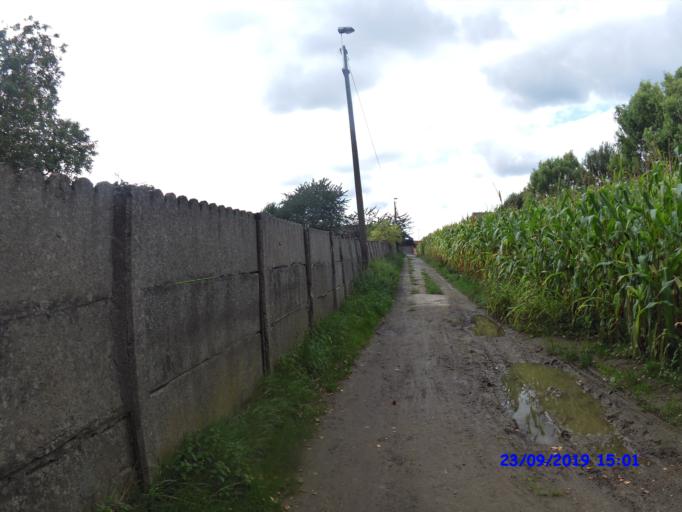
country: BE
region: Flanders
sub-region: Provincie Oost-Vlaanderen
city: Haaltert
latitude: 50.9108
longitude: 3.9751
